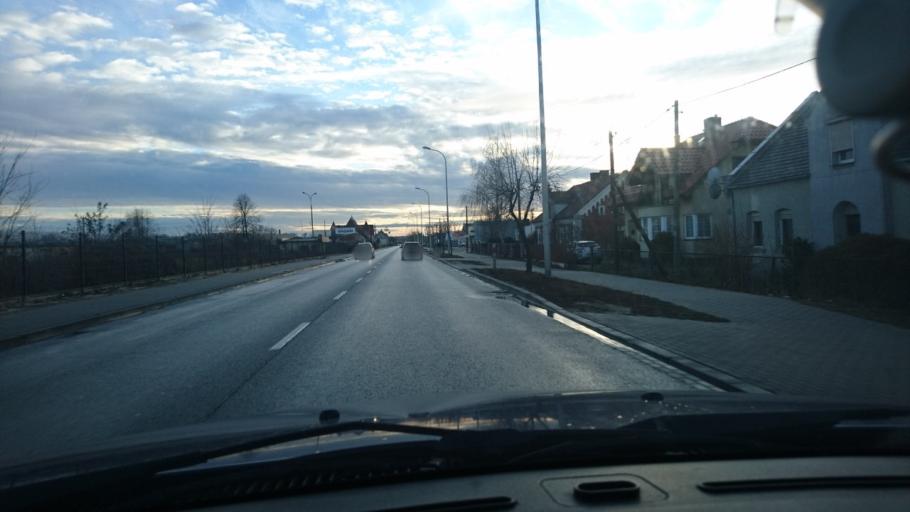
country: PL
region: Greater Poland Voivodeship
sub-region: Powiat kepinski
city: Kepno
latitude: 51.2950
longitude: 17.9963
